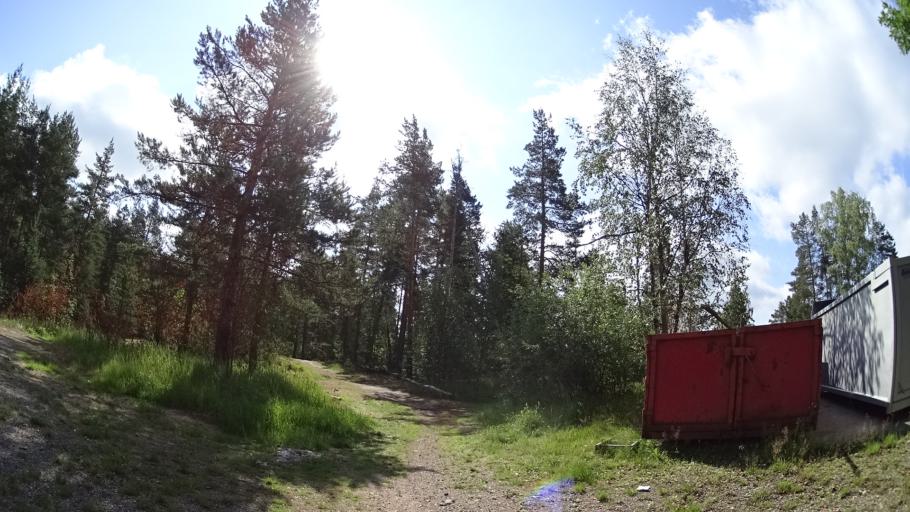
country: FI
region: Uusimaa
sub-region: Helsinki
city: Teekkarikylae
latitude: 60.2874
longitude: 24.9038
